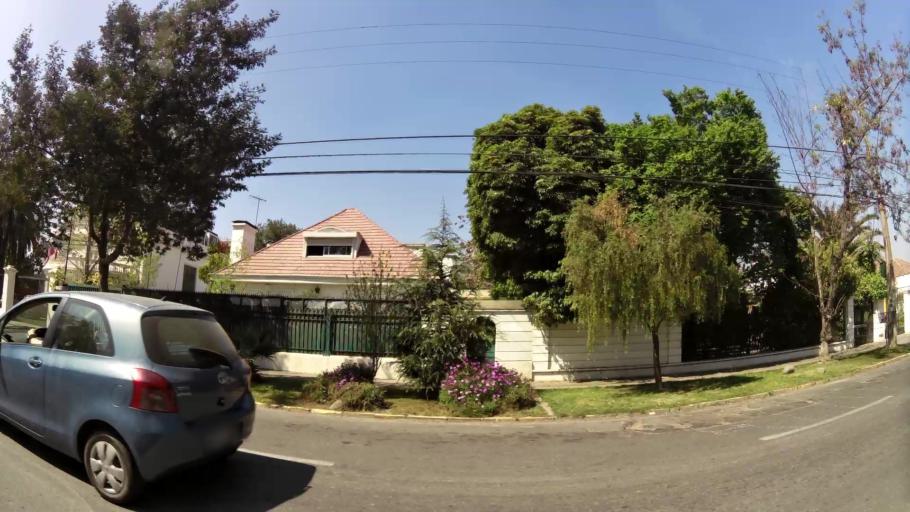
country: CL
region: Santiago Metropolitan
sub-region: Provincia de Santiago
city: Villa Presidente Frei, Nunoa, Santiago, Chile
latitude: -33.4558
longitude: -70.5800
